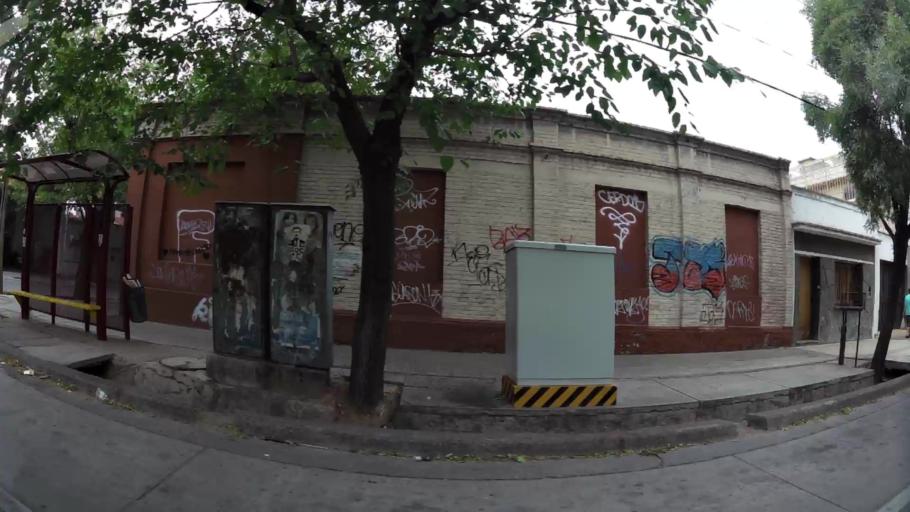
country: AR
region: Mendoza
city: Mendoza
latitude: -32.8940
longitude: -68.8590
